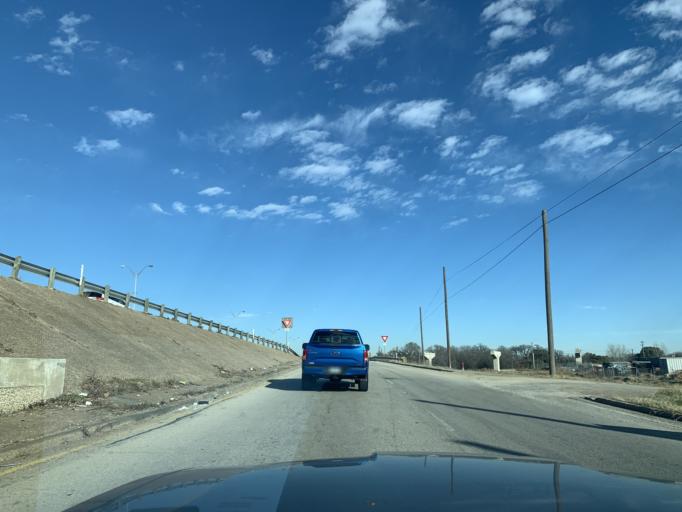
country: US
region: Texas
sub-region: Tarrant County
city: Arlington
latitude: 32.7583
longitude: -97.0630
